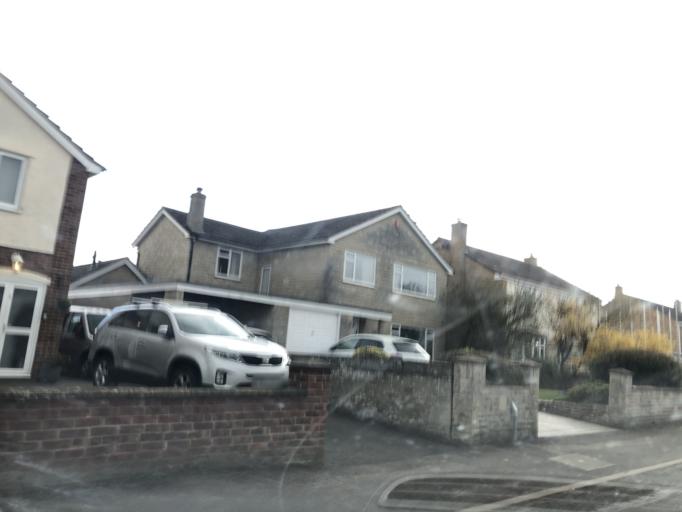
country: GB
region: England
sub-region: Oxfordshire
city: Bicester
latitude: 51.8978
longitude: -1.1660
